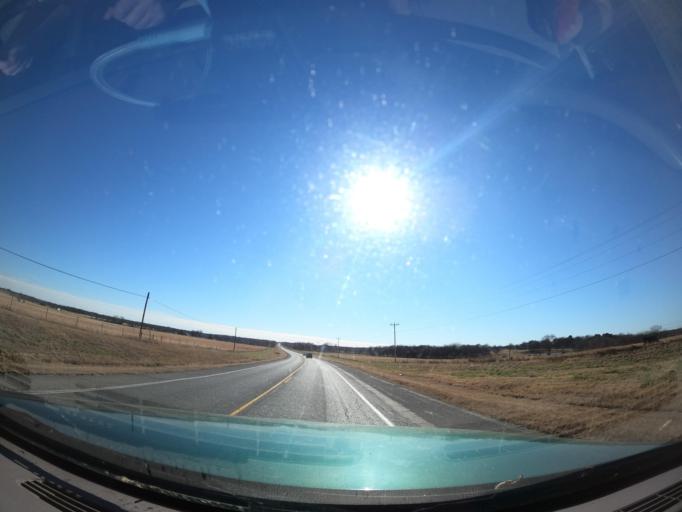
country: US
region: Oklahoma
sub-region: Muskogee County
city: Haskell
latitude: 35.8616
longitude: -95.6773
